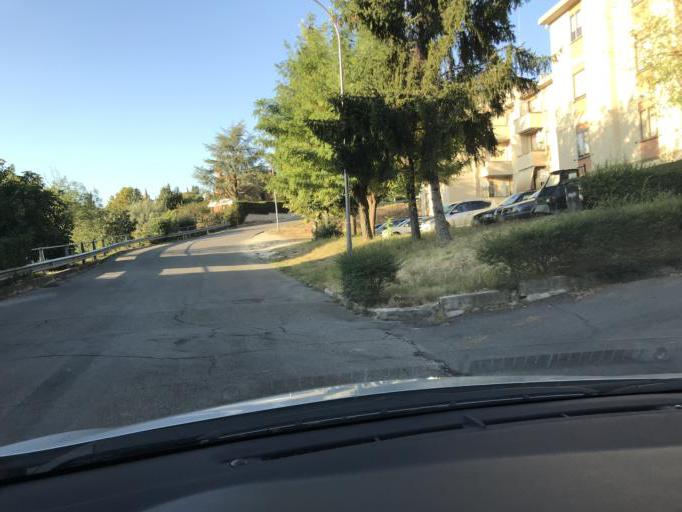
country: IT
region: Umbria
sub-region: Provincia di Terni
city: Amelia
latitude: 42.5489
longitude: 12.4172
